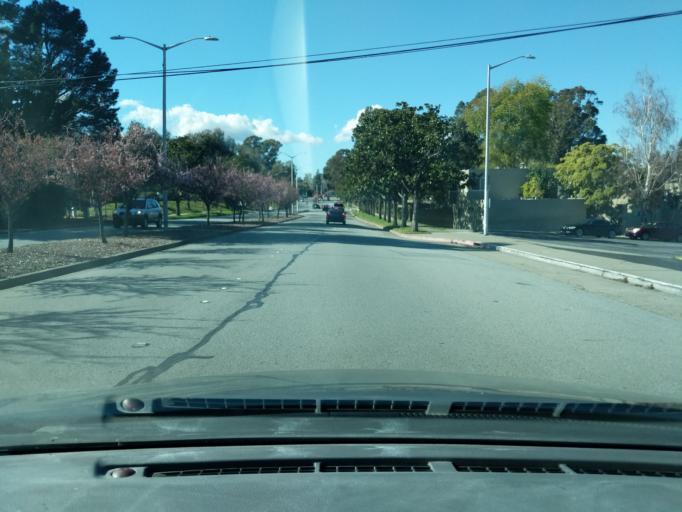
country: US
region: California
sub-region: San Mateo County
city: San Mateo
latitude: 37.5446
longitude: -122.3194
